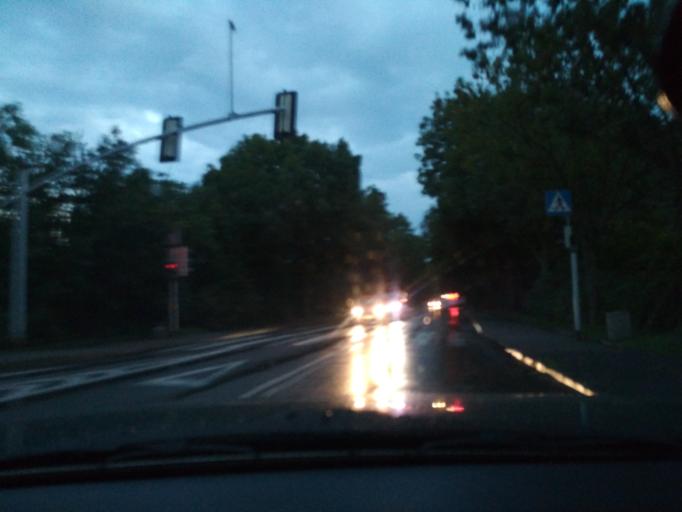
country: PL
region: Silesian Voivodeship
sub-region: Gliwice
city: Gliwice
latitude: 50.3014
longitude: 18.6590
